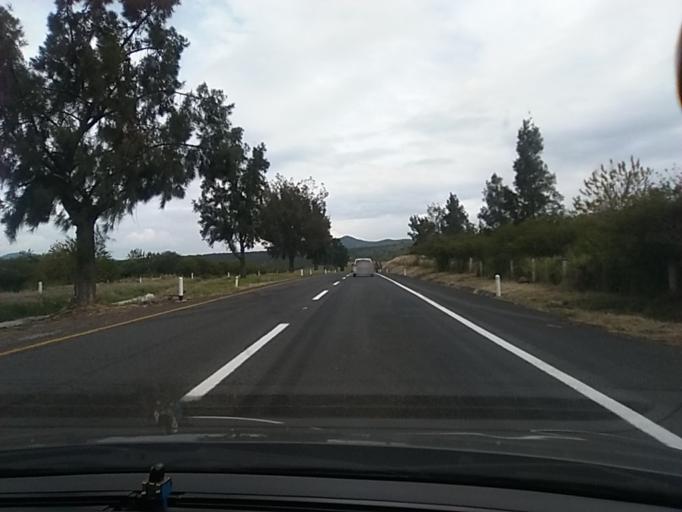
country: MX
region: Michoacan
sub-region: Vista Hermosa
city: La Angostura
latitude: 20.2430
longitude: -102.4073
